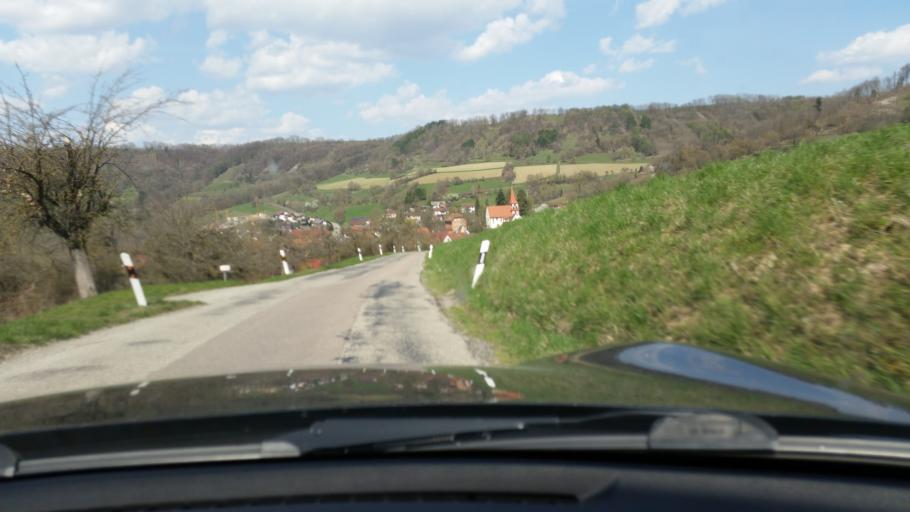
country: DE
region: Baden-Wuerttemberg
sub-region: Regierungsbezirk Stuttgart
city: Braunsbach
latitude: 49.2618
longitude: 9.7609
